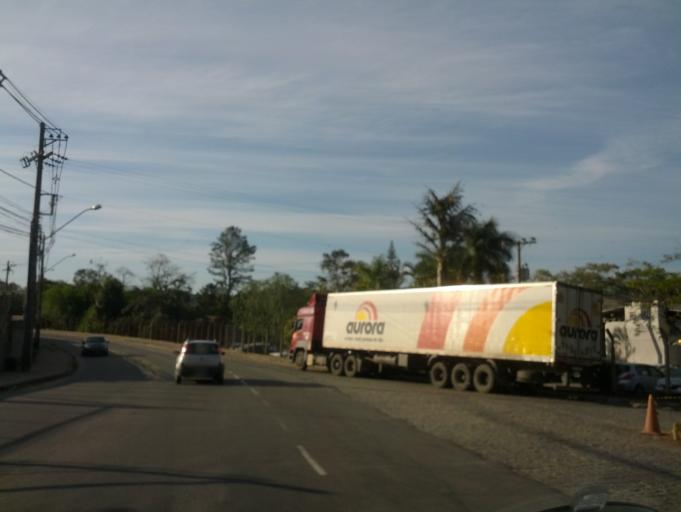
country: BR
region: Santa Catarina
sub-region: Indaial
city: Indaial
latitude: -26.9051
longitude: -49.1493
